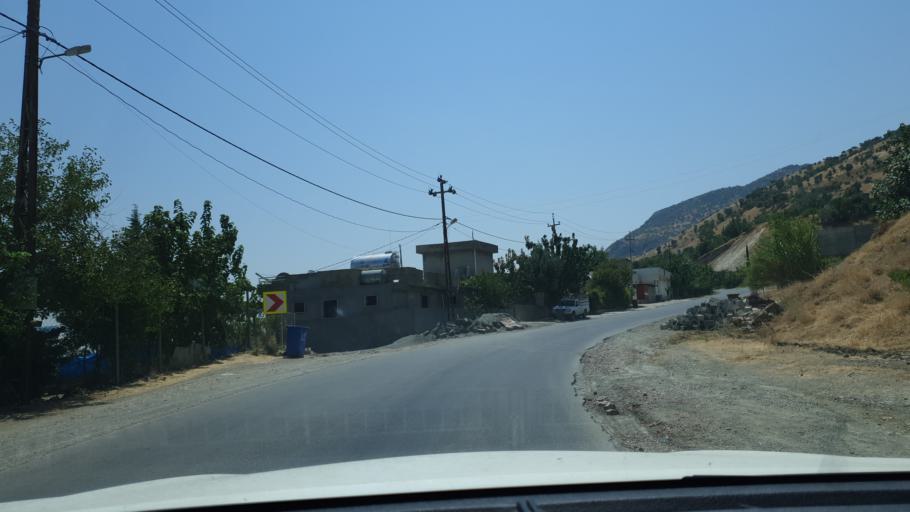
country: IQ
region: Arbil
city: Nahiyat Hiran
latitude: 36.2886
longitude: 44.4850
